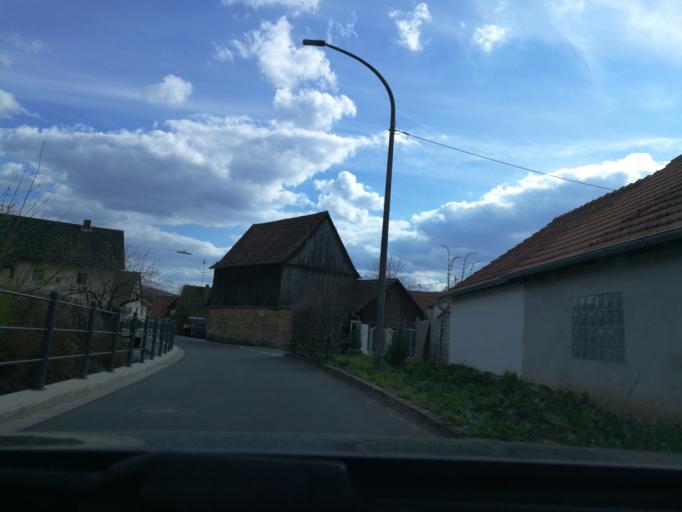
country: DE
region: Bavaria
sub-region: Upper Franconia
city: Heiligenstadt
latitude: 49.8204
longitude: 11.1158
